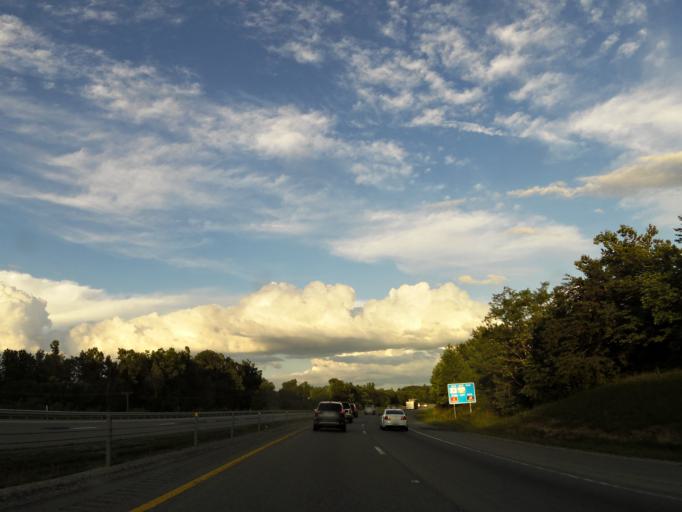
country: US
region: Tennessee
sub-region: Putnam County
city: Monterey
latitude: 36.1414
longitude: -85.3052
